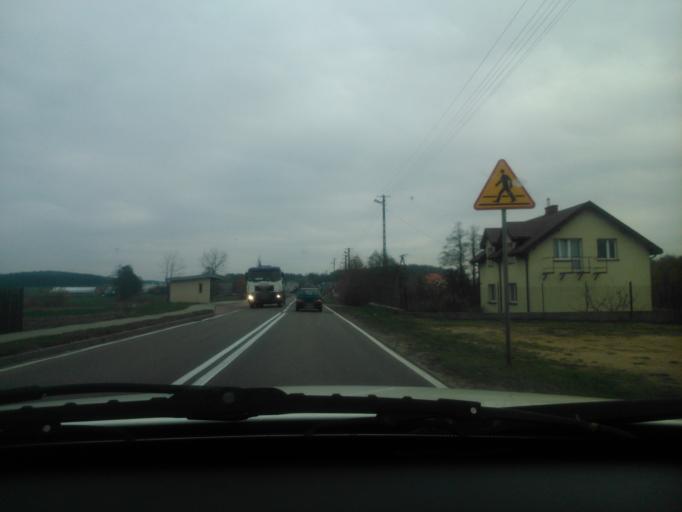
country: PL
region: Masovian Voivodeship
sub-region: Powiat mlawski
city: Lipowiec Koscielny
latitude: 53.1168
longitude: 20.2427
